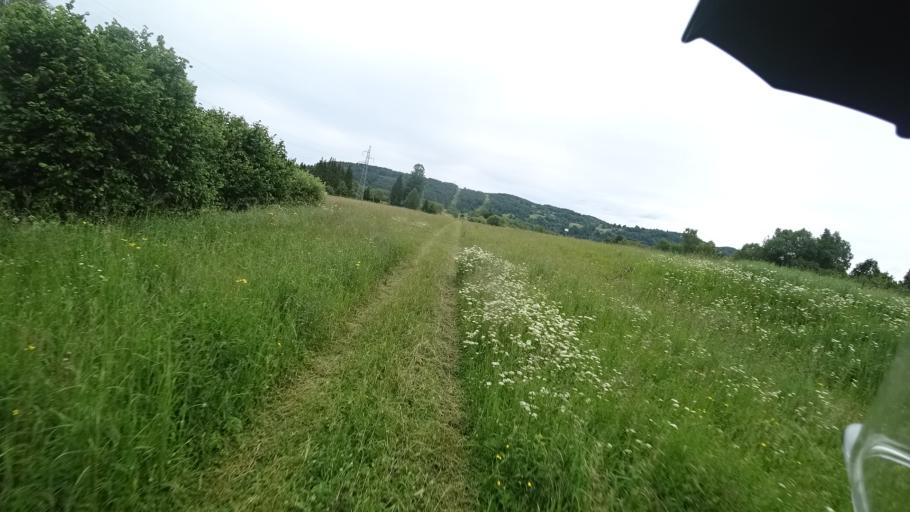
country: HR
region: Primorsko-Goranska
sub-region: Grad Delnice
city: Delnice
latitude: 45.3801
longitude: 14.8743
